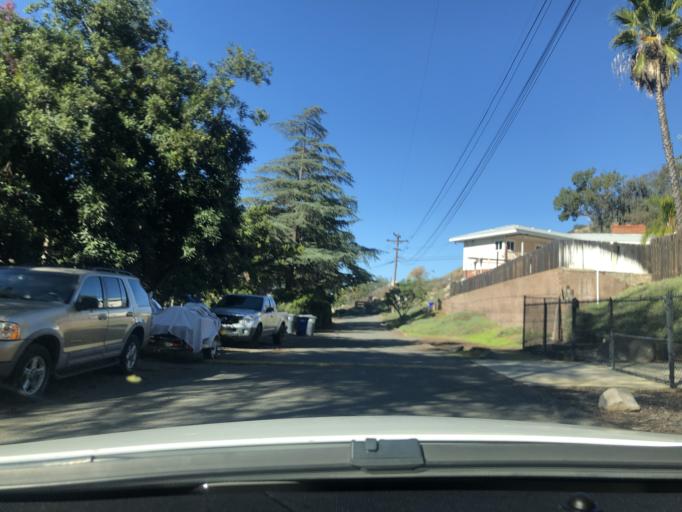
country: US
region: California
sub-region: San Diego County
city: El Cajon
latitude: 32.7826
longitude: -116.9438
